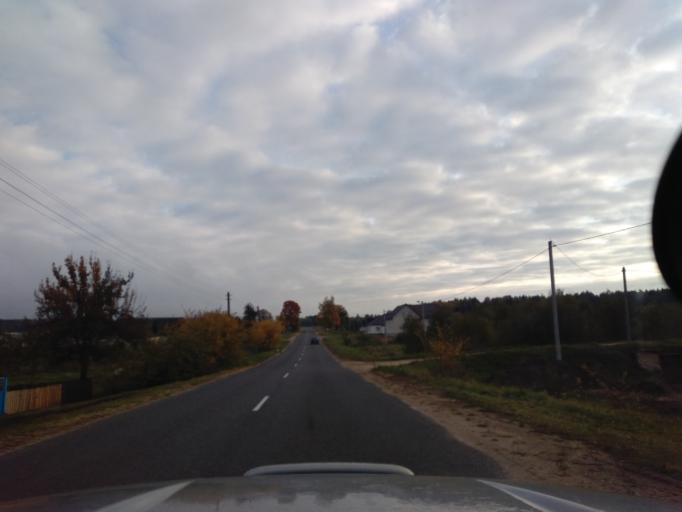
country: BY
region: Minsk
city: Kapyl'
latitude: 53.1624
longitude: 27.0989
